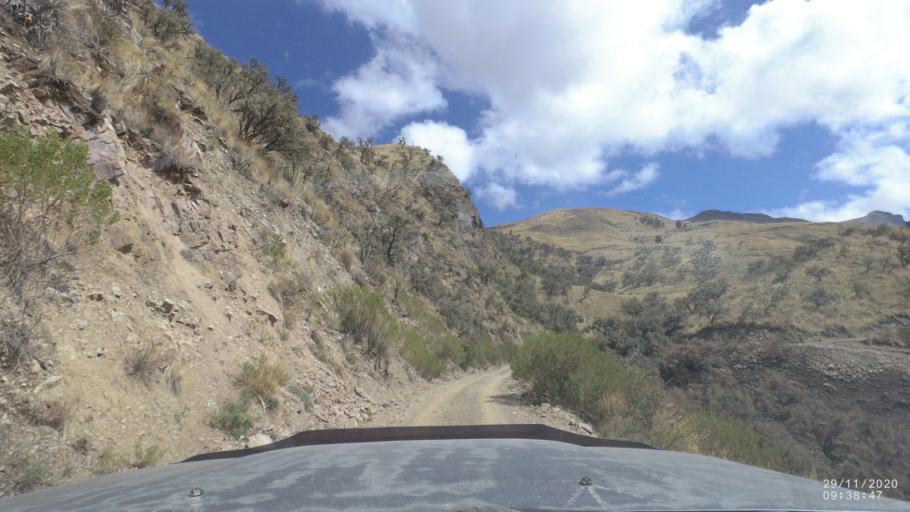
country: BO
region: Cochabamba
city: Cochabamba
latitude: -17.3061
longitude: -66.1847
